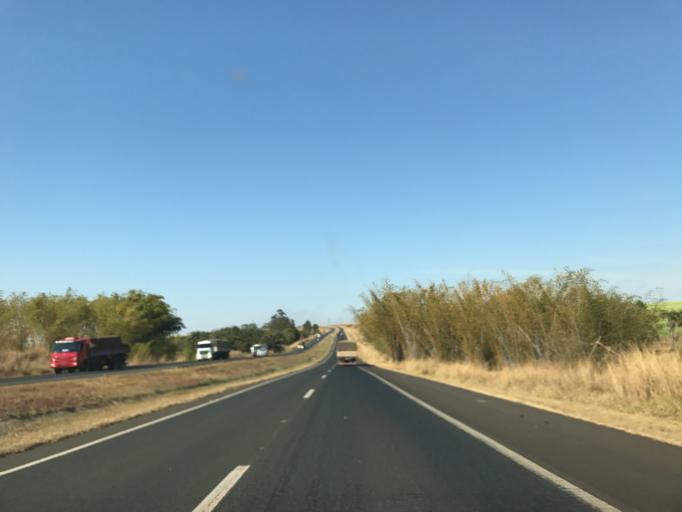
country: BR
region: Goias
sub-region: Goiatuba
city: Goiatuba
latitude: -17.8737
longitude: -49.2278
